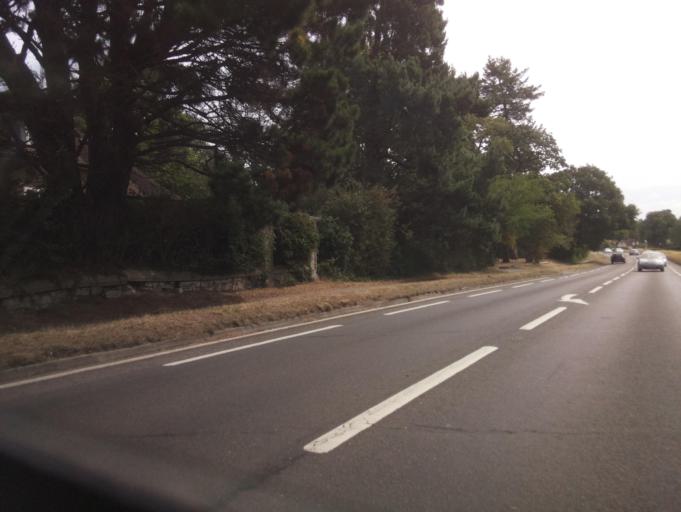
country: GB
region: England
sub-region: Surrey
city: Reigate
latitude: 51.2407
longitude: -0.2252
